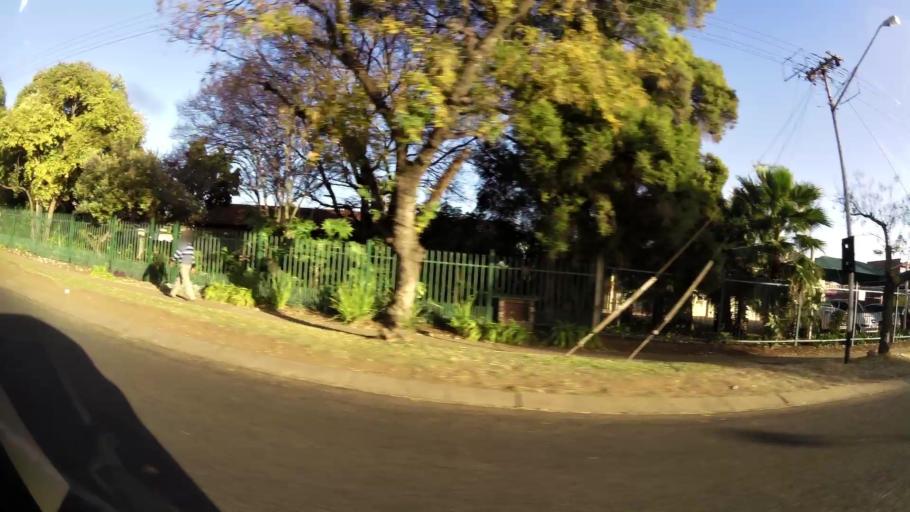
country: ZA
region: Gauteng
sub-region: City of Tshwane Metropolitan Municipality
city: Pretoria
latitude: -25.7045
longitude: 28.2395
